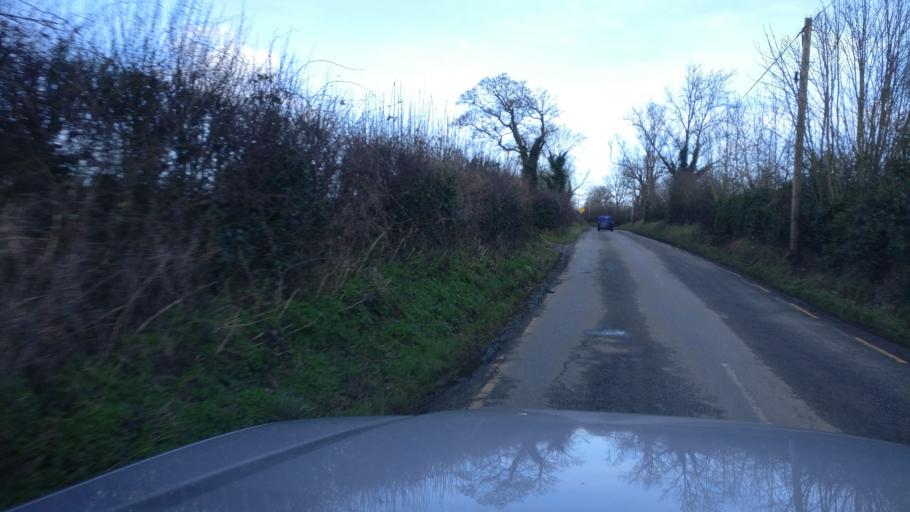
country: IE
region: Leinster
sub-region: Kilkenny
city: Castlecomer
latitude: 52.8349
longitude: -7.1941
